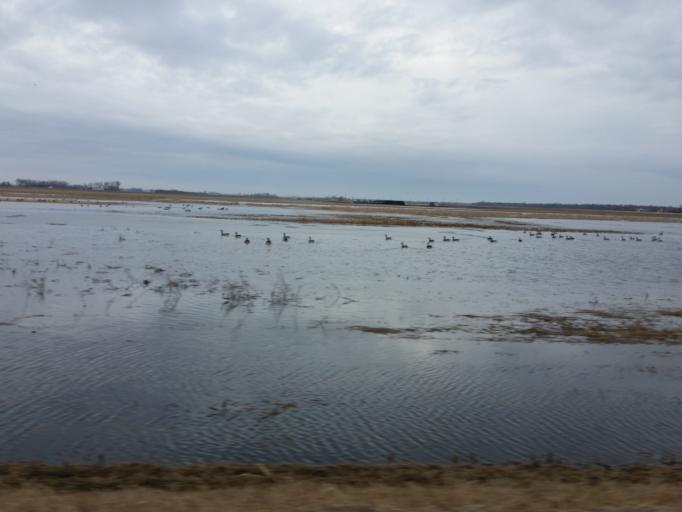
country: US
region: North Dakota
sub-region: Walsh County
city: Grafton
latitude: 48.4106
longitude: -97.4702
